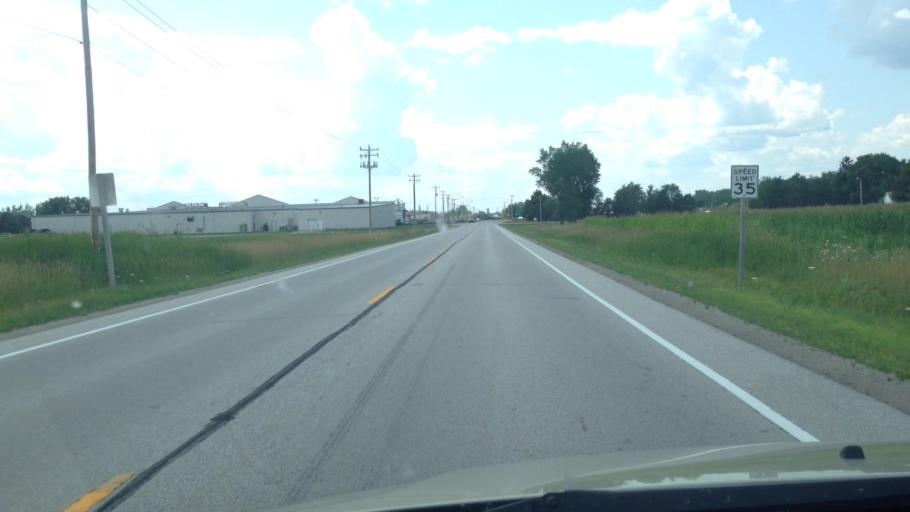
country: US
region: Wisconsin
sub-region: Brown County
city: Pulaski
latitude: 44.6574
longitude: -88.2153
